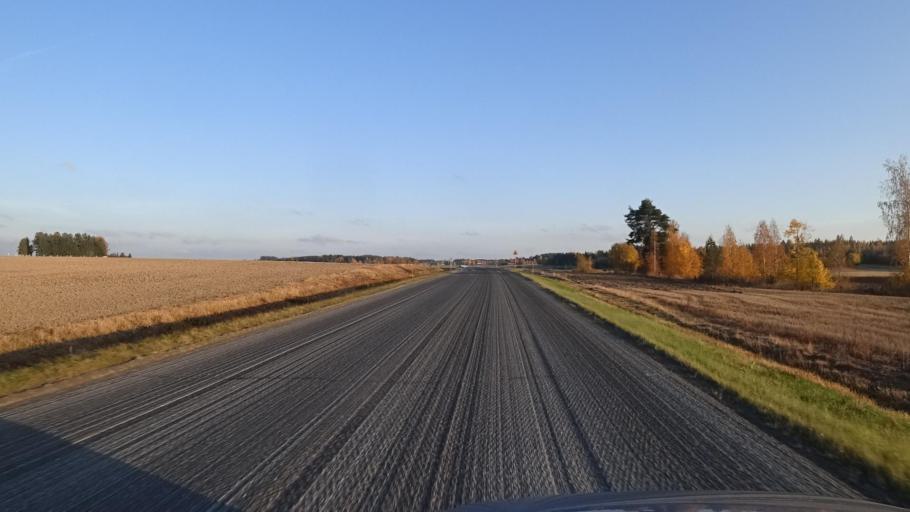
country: FI
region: Haeme
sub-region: Forssa
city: Ypaejae
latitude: 60.7888
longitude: 23.2910
